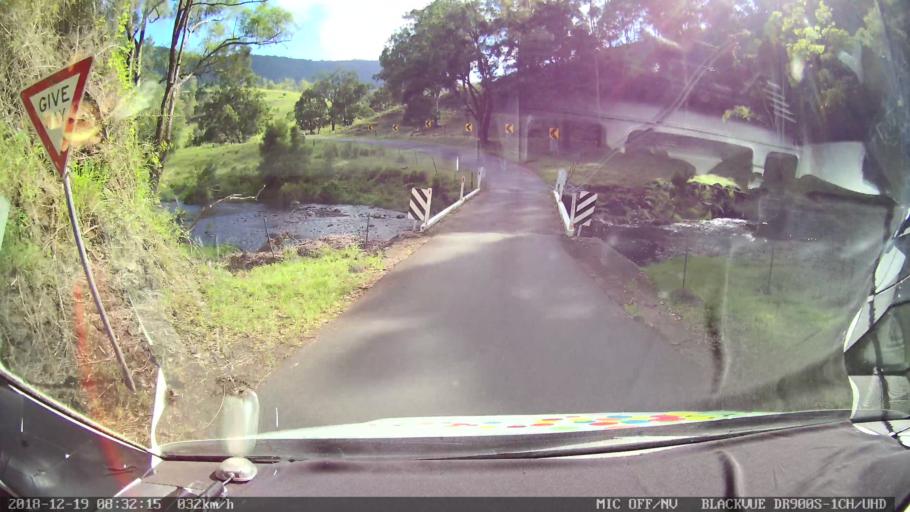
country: AU
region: New South Wales
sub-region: Kyogle
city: Kyogle
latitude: -28.3221
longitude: 152.9415
